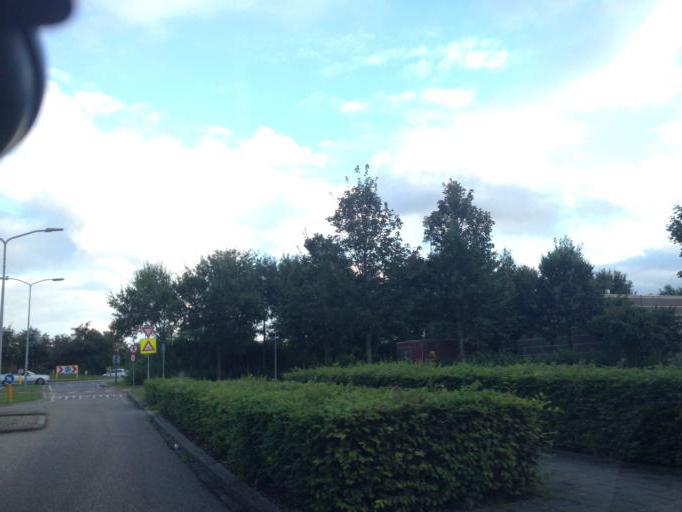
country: NL
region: Flevoland
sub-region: Gemeente Almere
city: Almere Stad
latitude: 52.3694
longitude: 5.2555
